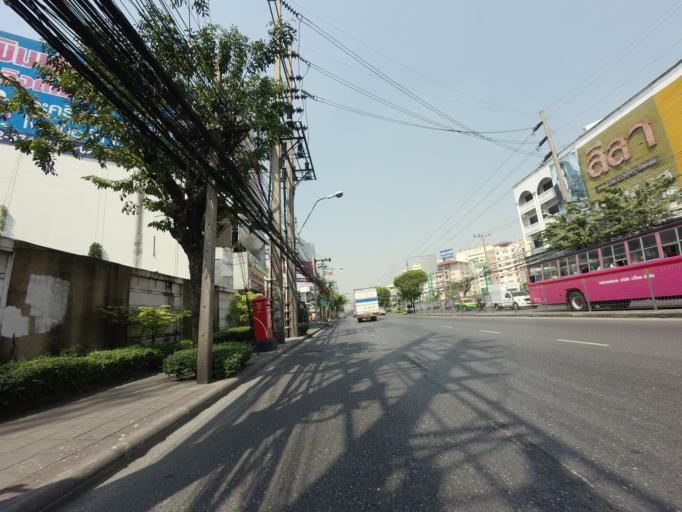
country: TH
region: Bangkok
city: Bang Kapi
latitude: 13.7698
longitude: 100.6383
